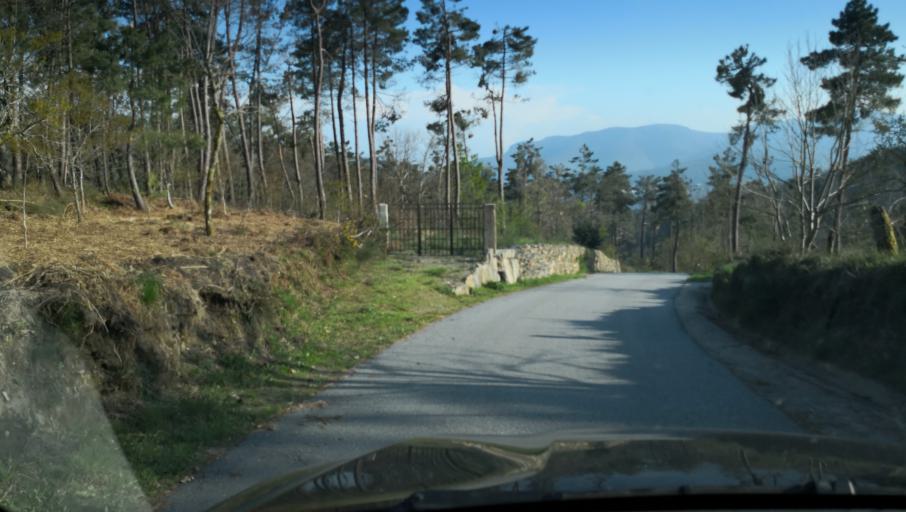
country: PT
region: Vila Real
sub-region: Vila Real
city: Vila Real
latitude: 41.3158
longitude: -7.8631
